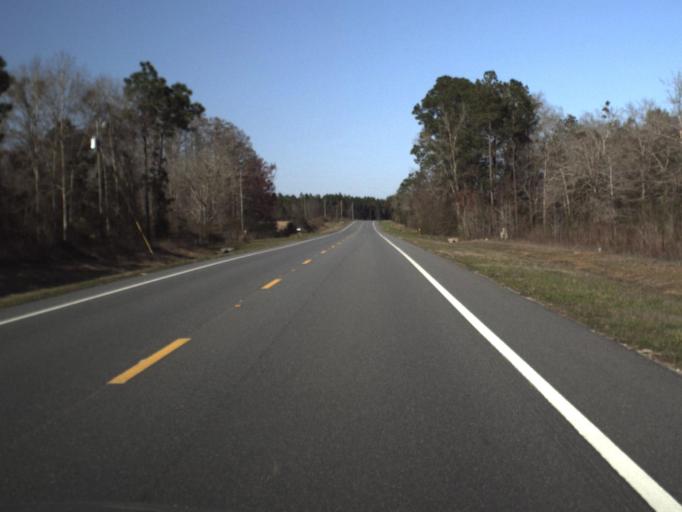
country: US
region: Florida
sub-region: Calhoun County
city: Blountstown
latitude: 30.4070
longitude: -85.2102
